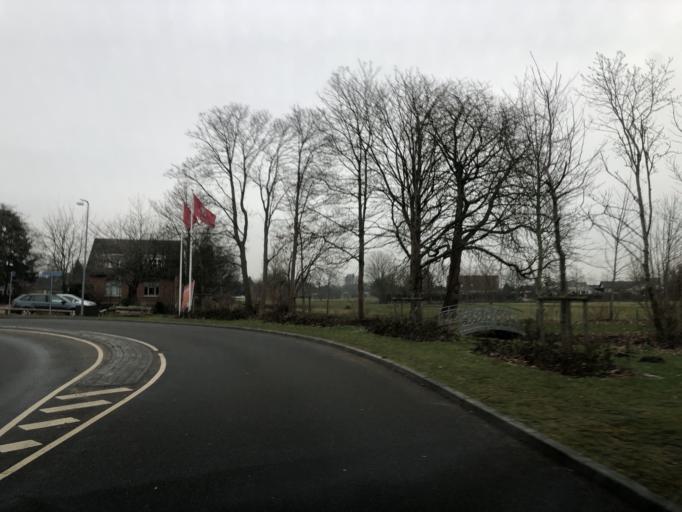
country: DK
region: South Denmark
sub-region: Faaborg-Midtfyn Kommune
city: Arslev
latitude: 55.3095
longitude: 10.4888
